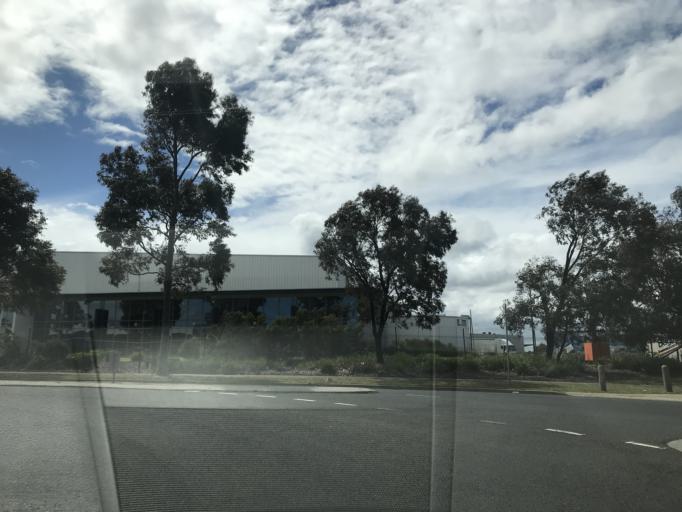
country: AU
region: Victoria
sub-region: Brimbank
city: Derrimut
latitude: -37.8090
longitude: 144.7663
